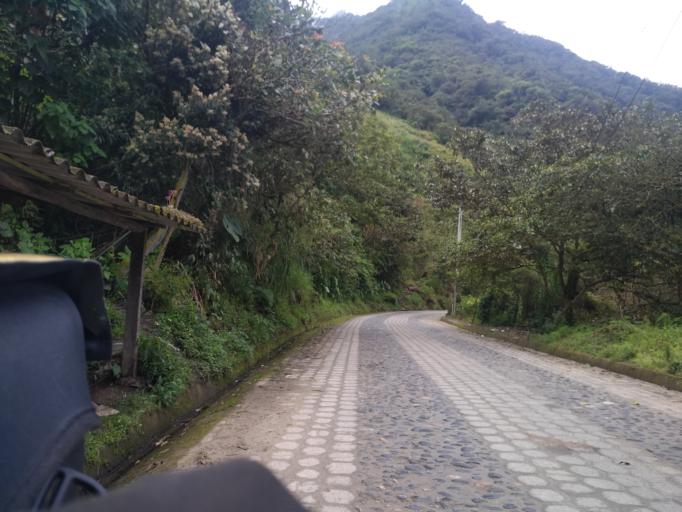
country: EC
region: Tungurahua
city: Banos
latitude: -1.4013
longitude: -78.2970
